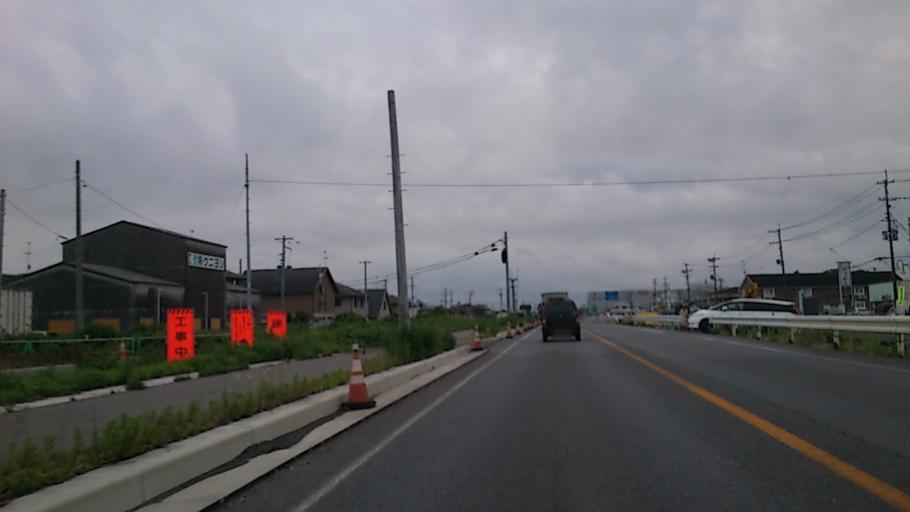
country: JP
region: Fukushima
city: Sukagawa
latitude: 37.2578
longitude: 140.3459
